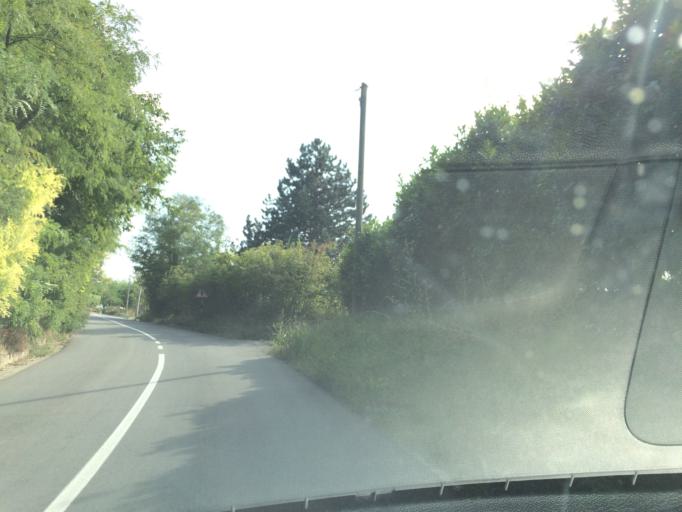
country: RS
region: Autonomna Pokrajina Vojvodina
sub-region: Juznobacki Okrug
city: Novi Sad
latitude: 45.1939
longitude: 19.8339
